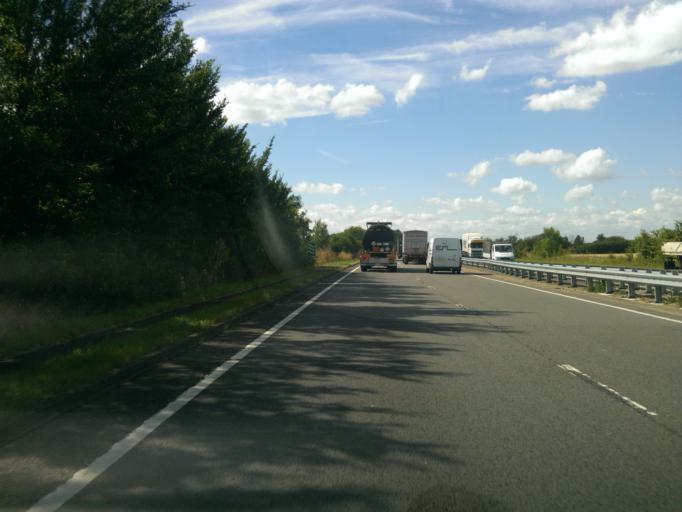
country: GB
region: England
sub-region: Cambridgeshire
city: Buckden
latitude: 52.3380
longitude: -0.3292
